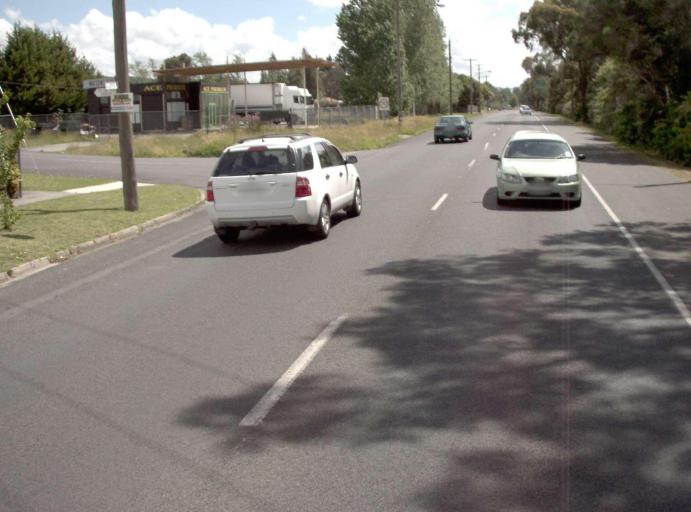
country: AU
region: Victoria
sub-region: Latrobe
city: Moe
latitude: -38.1828
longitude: 146.2418
